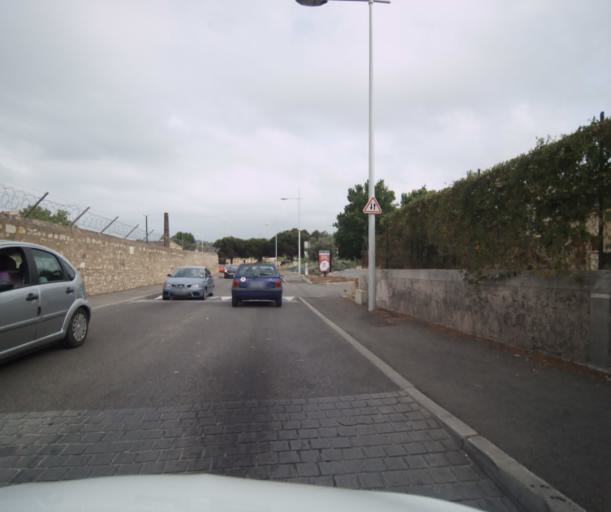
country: FR
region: Provence-Alpes-Cote d'Azur
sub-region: Departement du Var
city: La Seyne-sur-Mer
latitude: 43.1191
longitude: 5.8826
